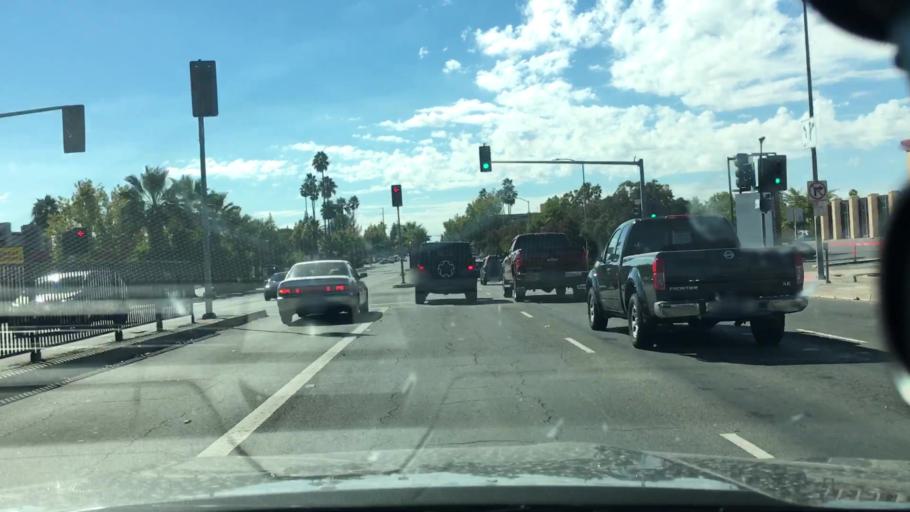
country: US
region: California
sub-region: Sacramento County
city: Arden-Arcade
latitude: 38.6090
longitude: -121.3830
